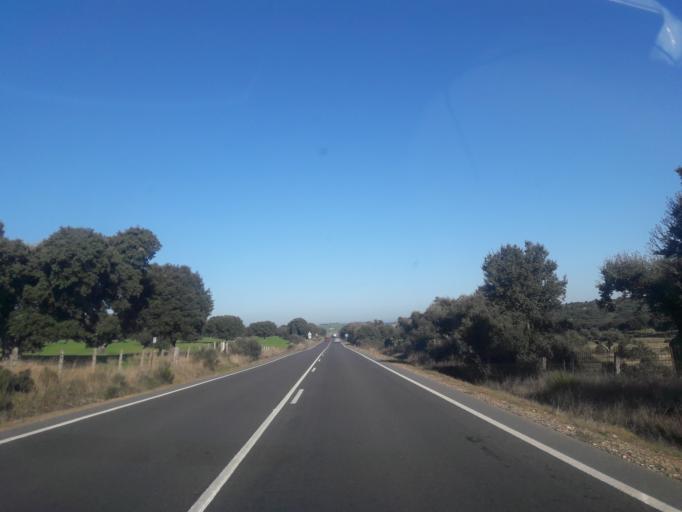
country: ES
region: Castille and Leon
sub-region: Provincia de Salamanca
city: Golpejas
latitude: 40.9897
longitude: -5.8786
